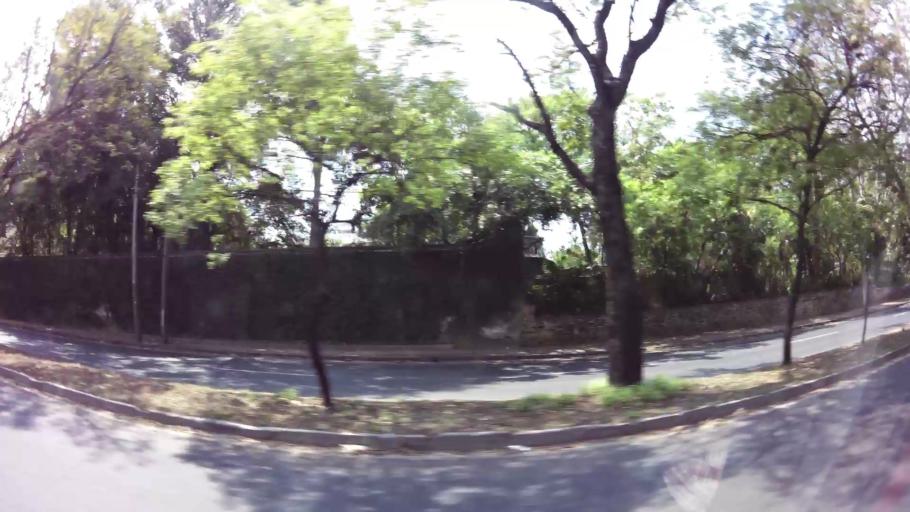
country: PY
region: Asuncion
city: Asuncion
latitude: -25.2794
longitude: -57.5866
